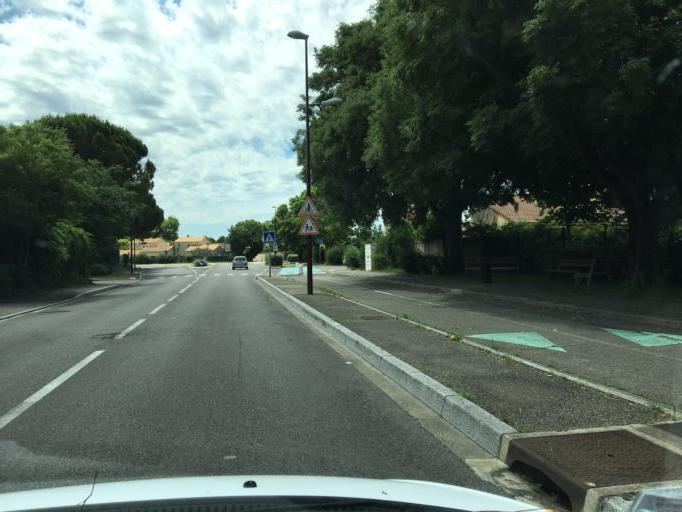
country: FR
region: Provence-Alpes-Cote d'Azur
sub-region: Departement du Vaucluse
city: Le Pontet
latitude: 43.9447
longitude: 4.8433
